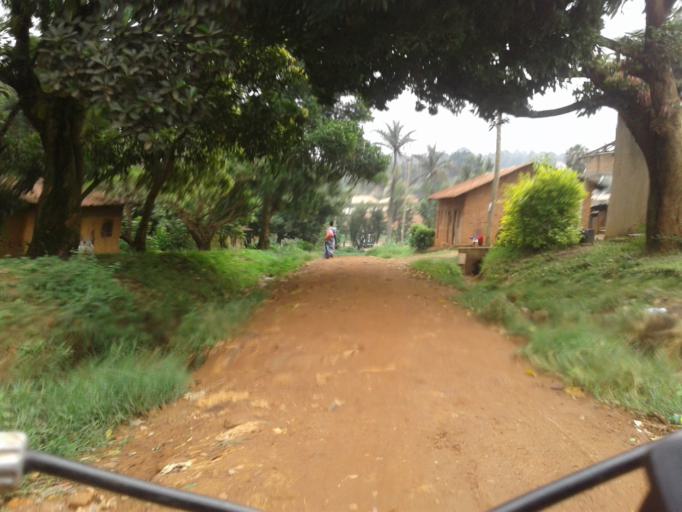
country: UG
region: Western Region
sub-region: Hoima District
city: Hoima
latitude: 1.4242
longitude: 31.3474
